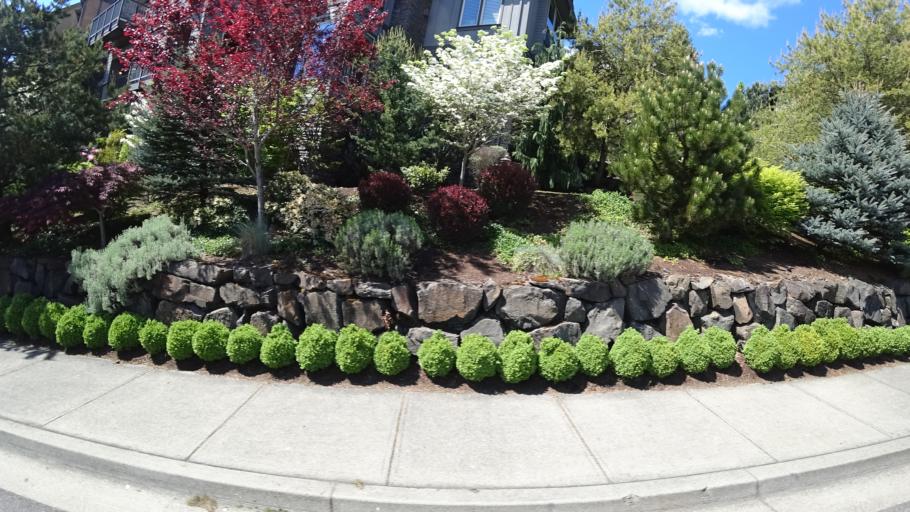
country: US
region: Oregon
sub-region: Washington County
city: West Haven
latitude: 45.5493
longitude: -122.7787
